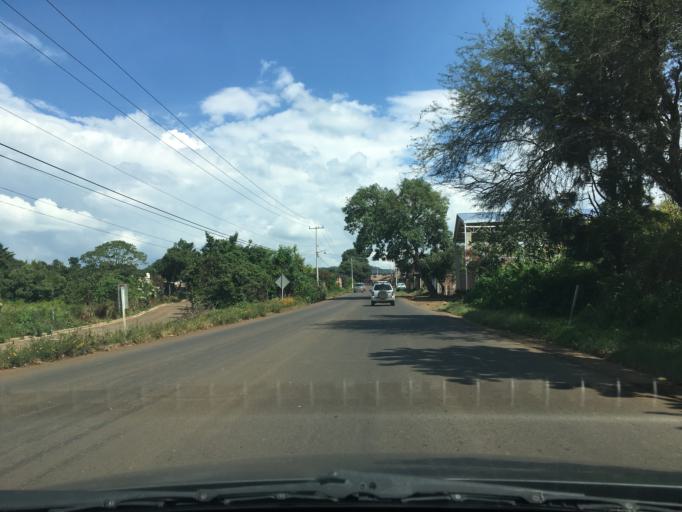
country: MX
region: Michoacan
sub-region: Tingueindin
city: Tingueindin
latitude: 19.8432
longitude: -102.4736
